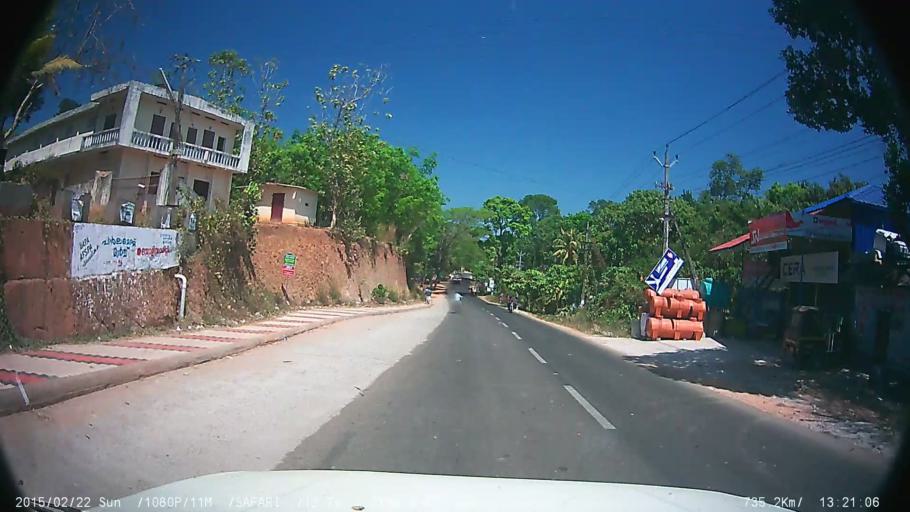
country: IN
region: Kerala
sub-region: Kottayam
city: Changanacheri
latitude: 9.4760
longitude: 76.5797
